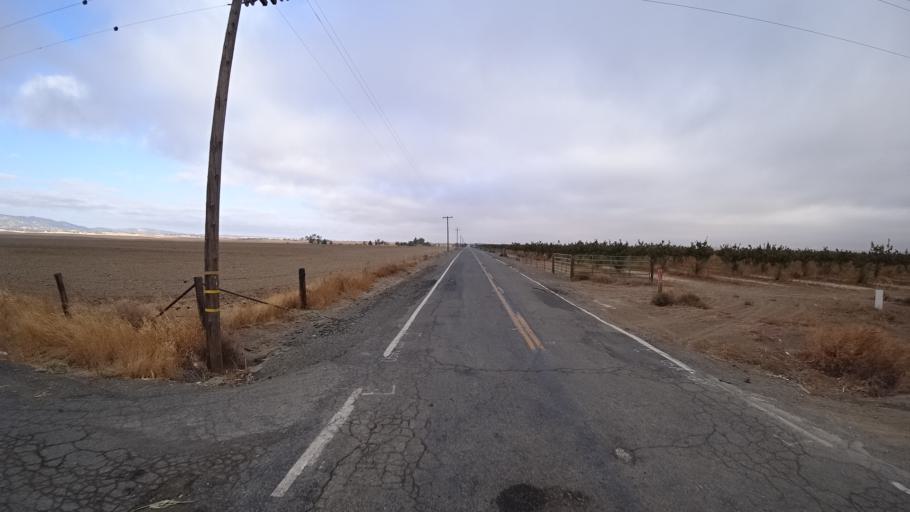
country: US
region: California
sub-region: Yolo County
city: Esparto
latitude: 38.7957
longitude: -122.0437
